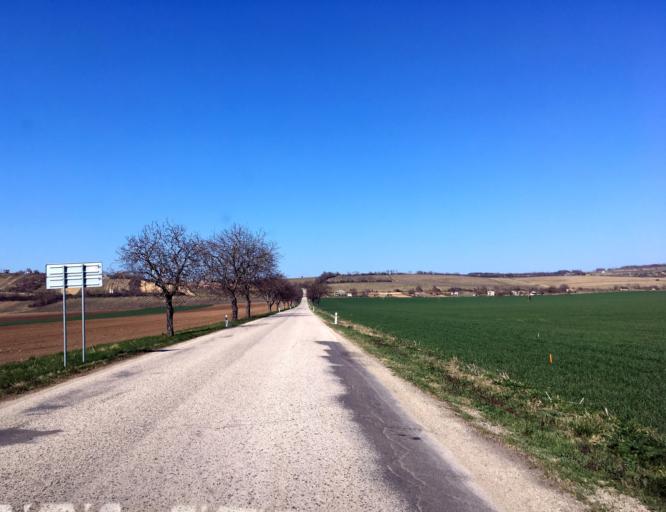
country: HU
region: Komarom-Esztergom
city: Nyergesujfalu
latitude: 47.8126
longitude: 18.6019
